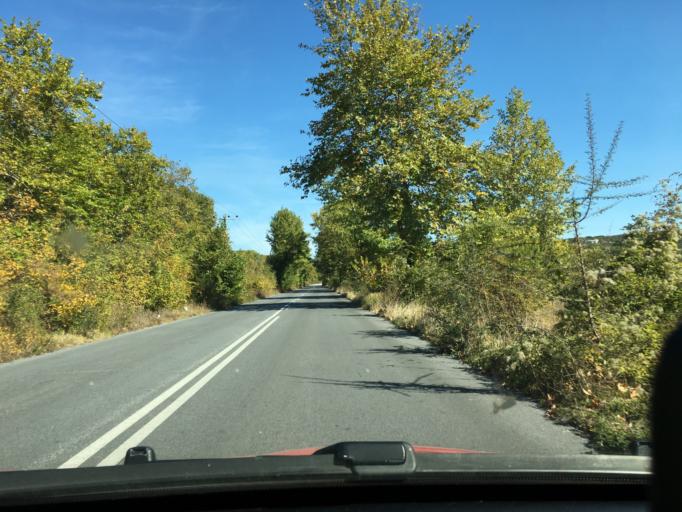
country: GR
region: Central Macedonia
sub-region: Nomos Chalkidikis
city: Megali Panagia
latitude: 40.3789
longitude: 23.6979
